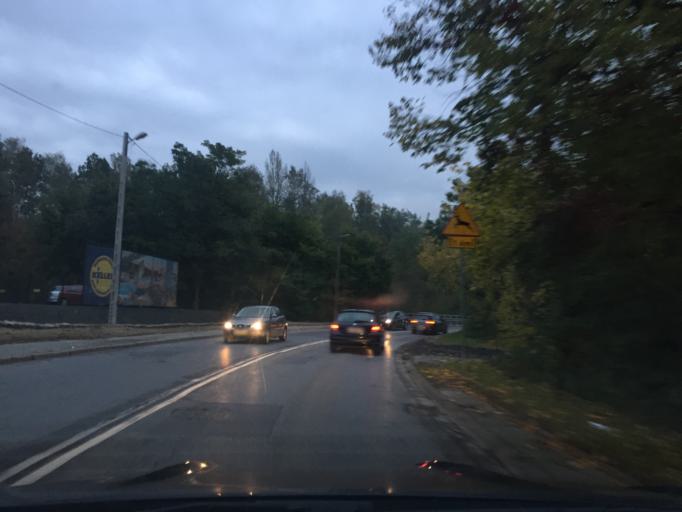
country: PL
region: Lesser Poland Voivodeship
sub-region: Powiat krakowski
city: Wrzasowice
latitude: 50.0079
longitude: 19.9362
